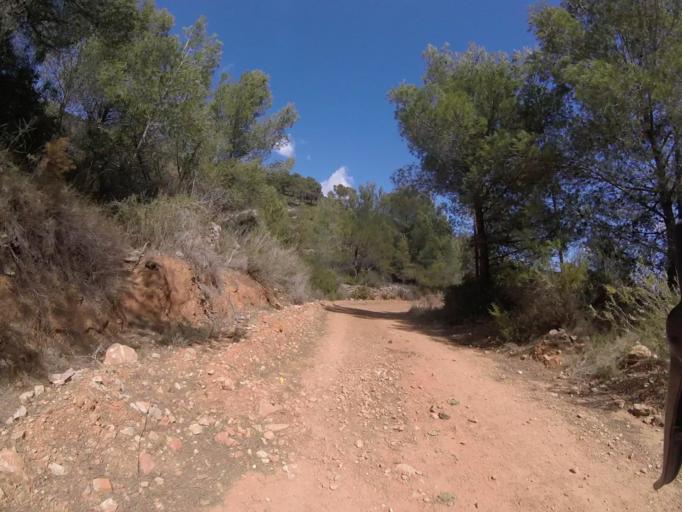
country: ES
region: Valencia
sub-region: Provincia de Castello
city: Orpesa/Oropesa del Mar
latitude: 40.1649
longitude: 0.1193
